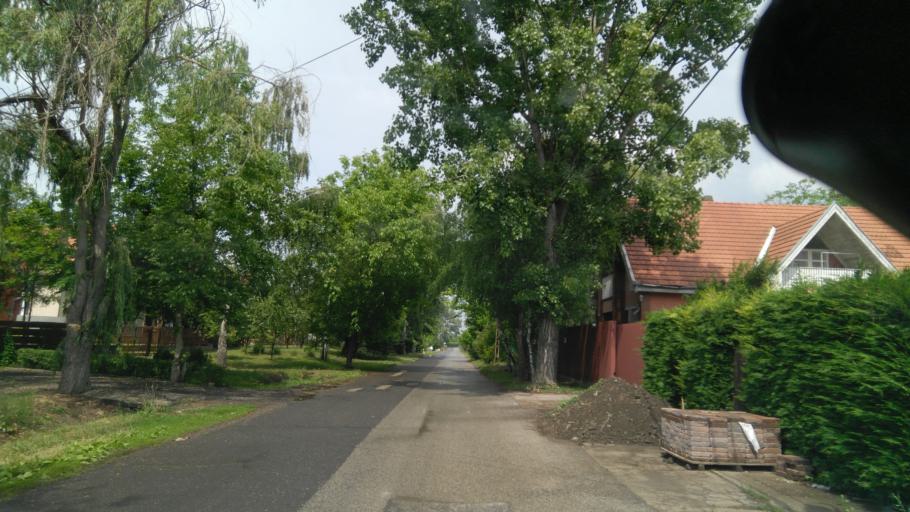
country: HU
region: Bekes
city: Bekescsaba
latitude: 46.6675
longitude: 21.1741
